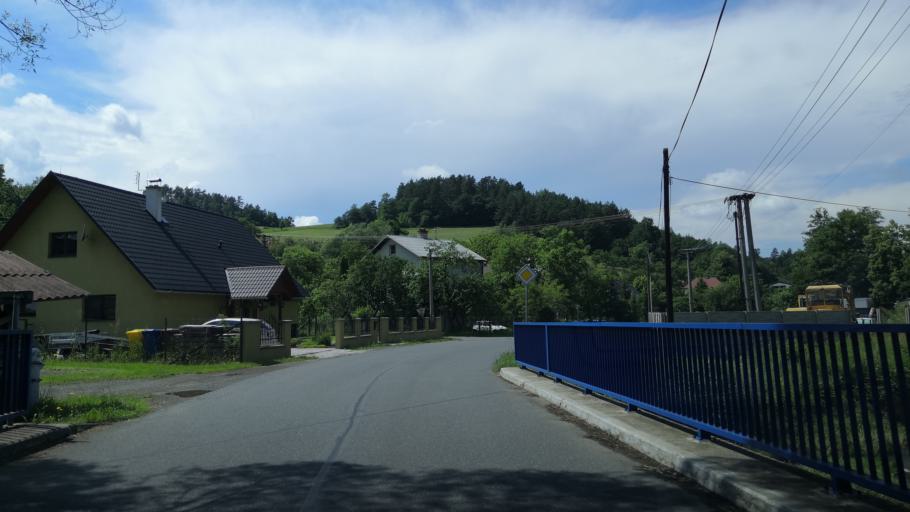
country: CZ
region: Zlin
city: Vidce
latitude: 49.4447
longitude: 18.0810
